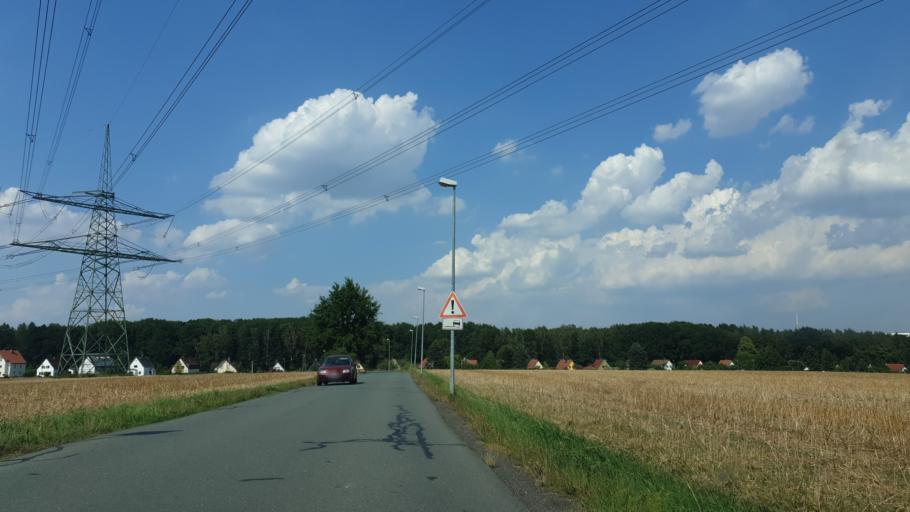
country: DE
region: Saxony
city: Neukirchen
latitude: 50.7785
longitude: 12.8869
